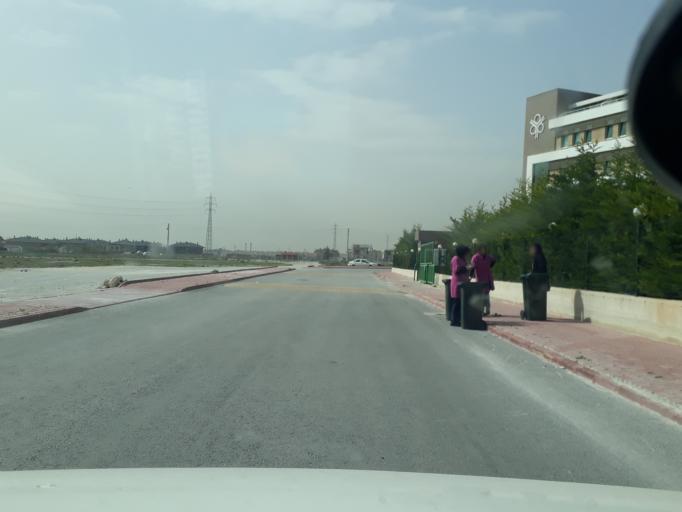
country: TR
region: Konya
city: Sille
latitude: 37.9461
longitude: 32.4756
